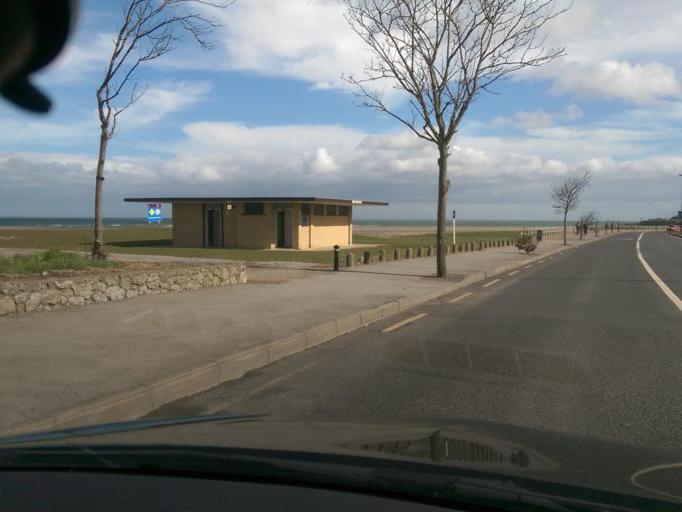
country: IE
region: Leinster
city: Malahide
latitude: 53.4487
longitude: -6.1373
